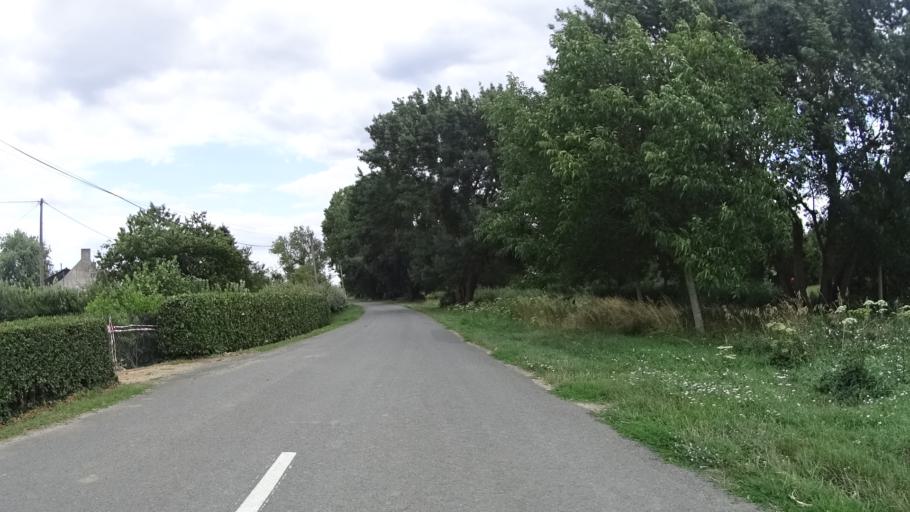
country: FR
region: Pays de la Loire
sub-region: Departement de Maine-et-Loire
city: Saint-Clement-des-Levees
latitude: 47.3544
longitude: -0.1719
